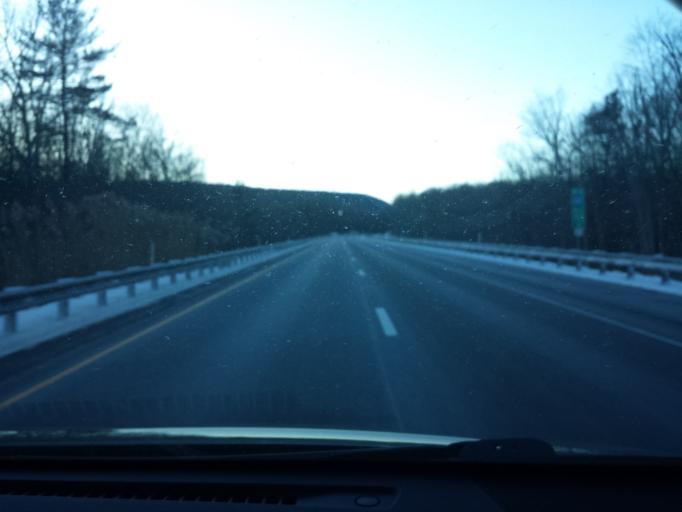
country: US
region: Pennsylvania
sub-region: Clinton County
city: Castanea
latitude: 41.0491
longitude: -77.3344
